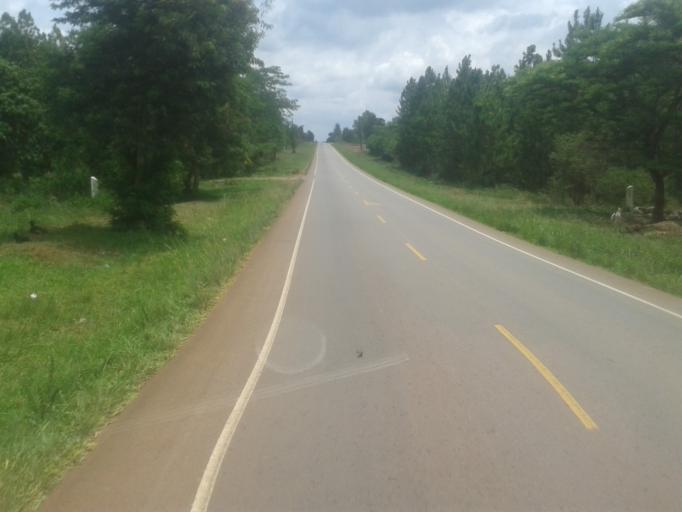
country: UG
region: Central Region
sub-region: Luwero District
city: Luwero
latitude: 1.0544
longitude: 32.4671
